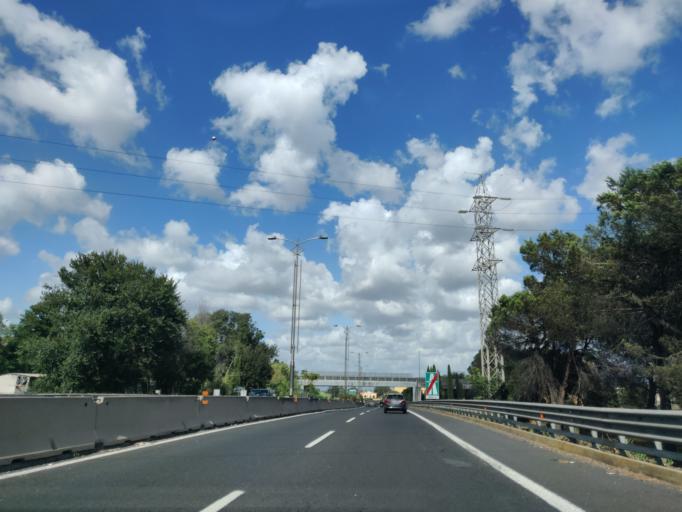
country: IT
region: Latium
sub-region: Citta metropolitana di Roma Capitale
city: Vitinia
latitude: 41.8325
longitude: 12.4430
